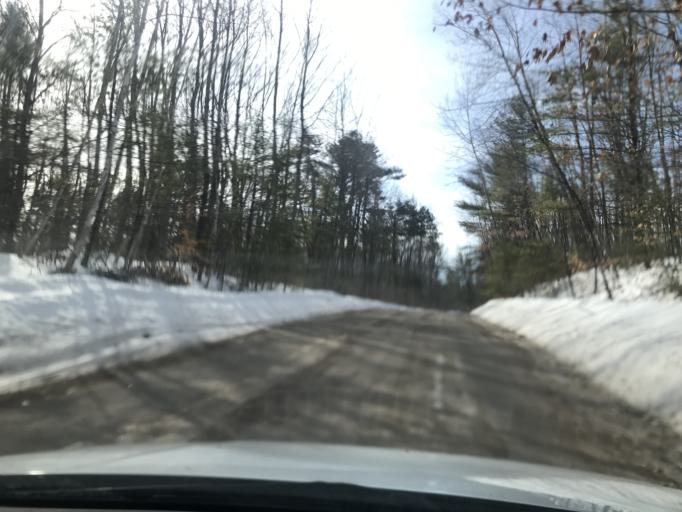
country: US
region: Wisconsin
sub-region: Menominee County
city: Legend Lake
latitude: 45.1154
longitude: -88.4342
